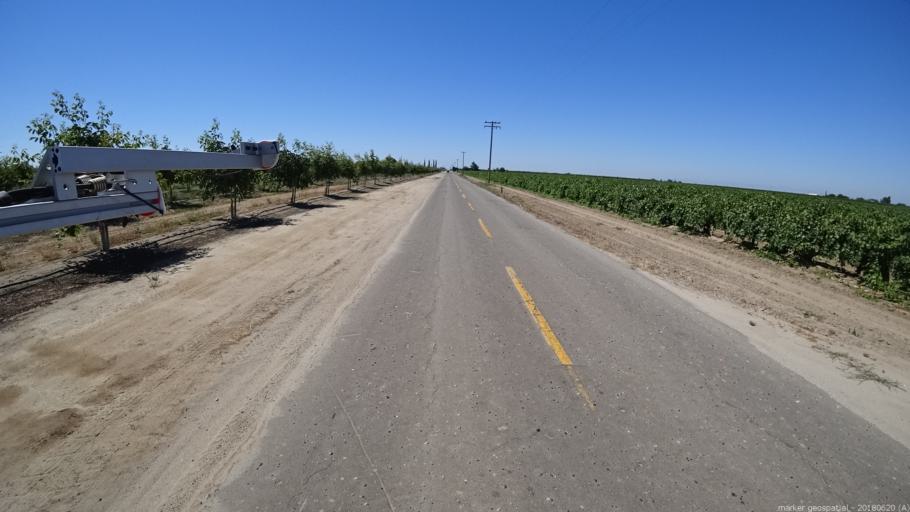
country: US
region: California
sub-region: Fresno County
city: Biola
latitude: 36.8500
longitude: -120.0101
